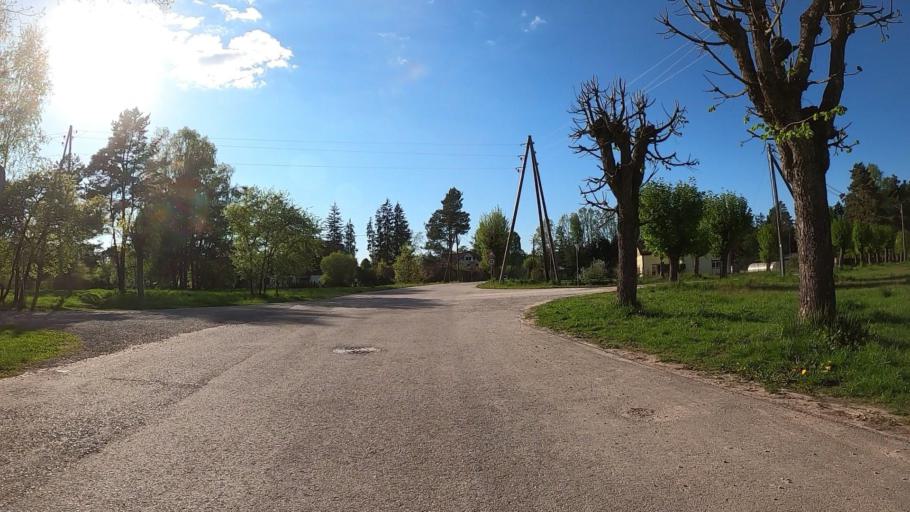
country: LV
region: Baldone
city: Baldone
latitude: 56.7443
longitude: 24.4011
